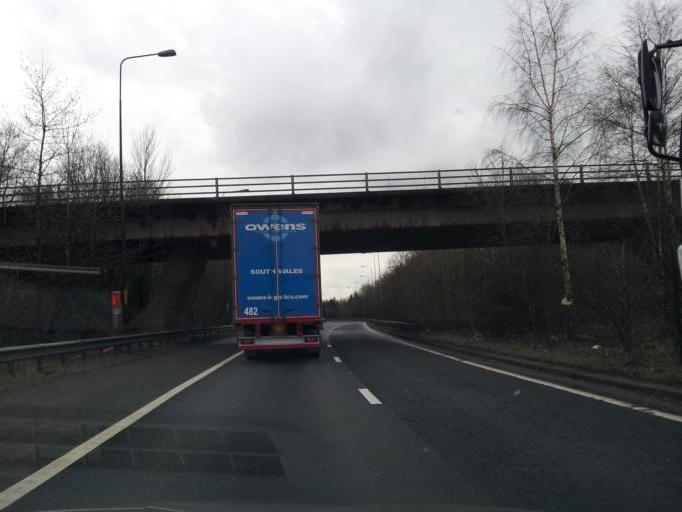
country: GB
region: England
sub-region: Warrington
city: Croft
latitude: 53.4265
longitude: -2.5454
